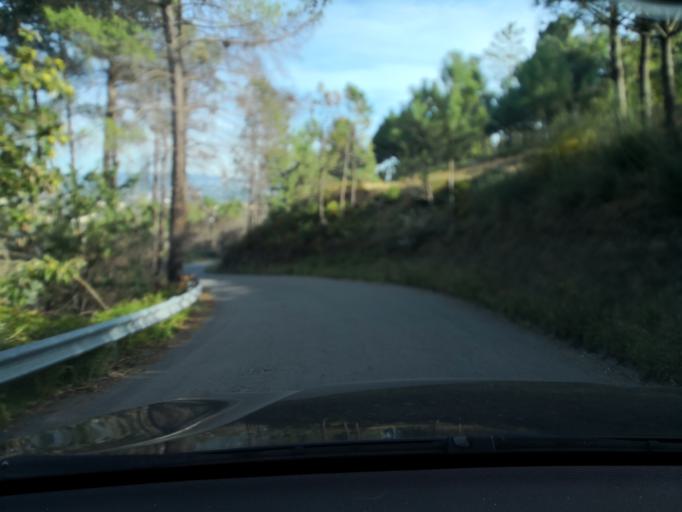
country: PT
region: Vila Real
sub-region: Vila Real
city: Vila Real
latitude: 41.3377
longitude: -7.7460
